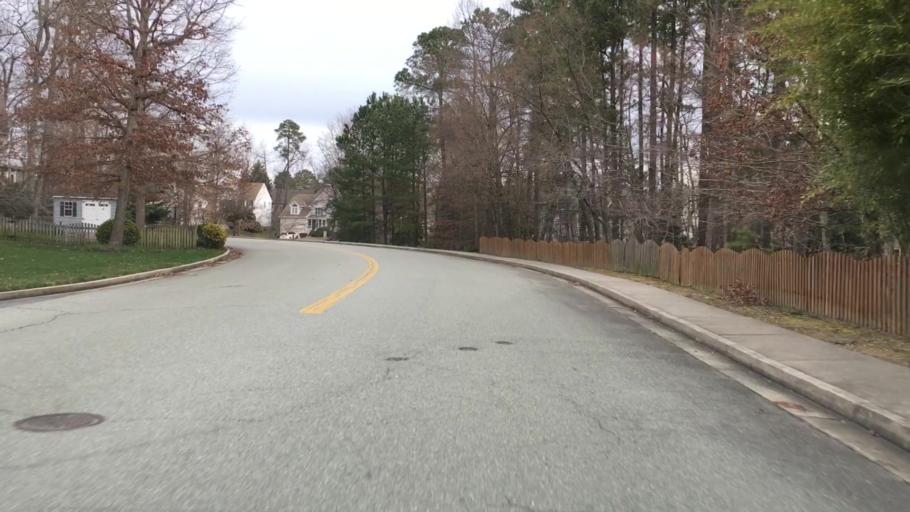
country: US
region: Virginia
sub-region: Henrico County
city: Short Pump
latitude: 37.6505
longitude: -77.5726
